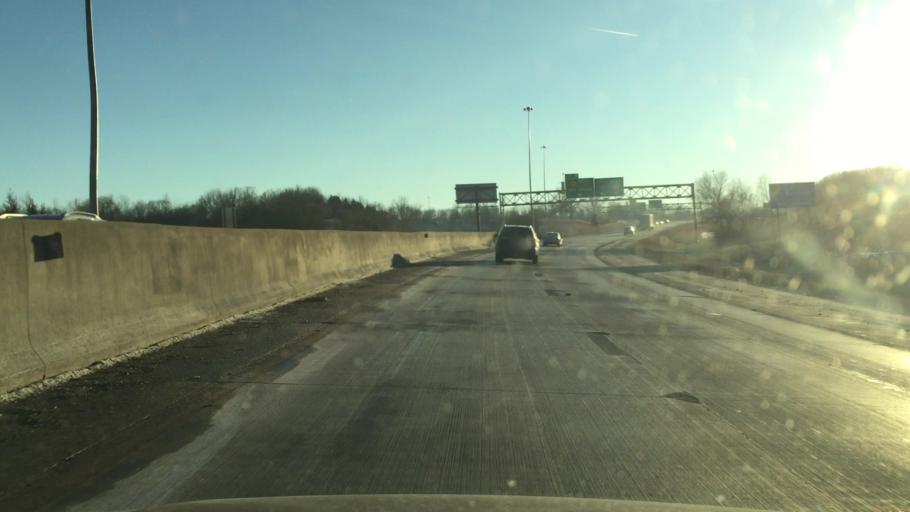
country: US
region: Kansas
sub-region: Wyandotte County
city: Kansas City
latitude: 39.1517
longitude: -94.6524
